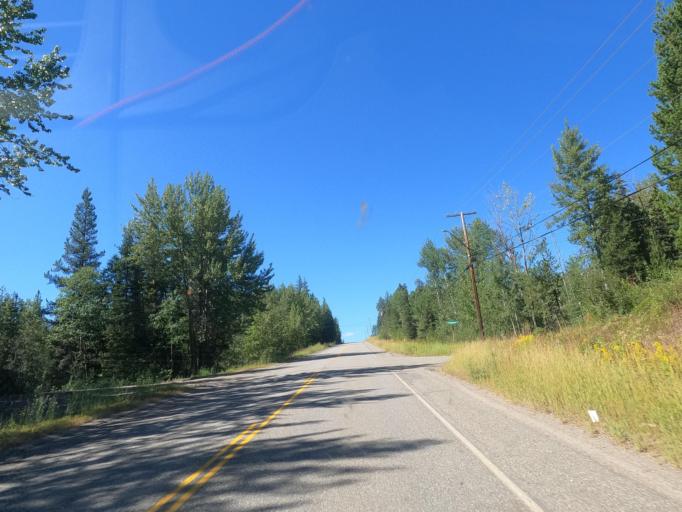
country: CA
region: British Columbia
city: Quesnel
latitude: 53.0302
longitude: -122.4156
